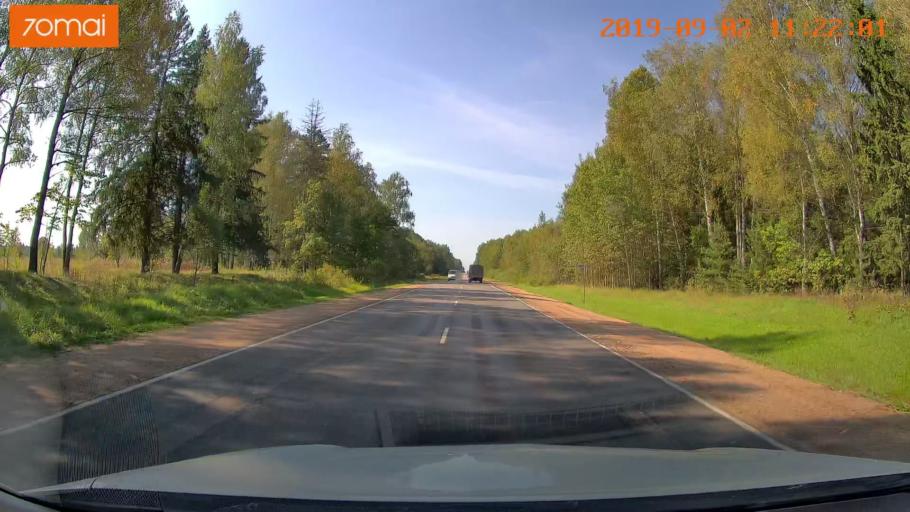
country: RU
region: Smolensk
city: Roslavl'
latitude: 54.0296
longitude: 33.0228
